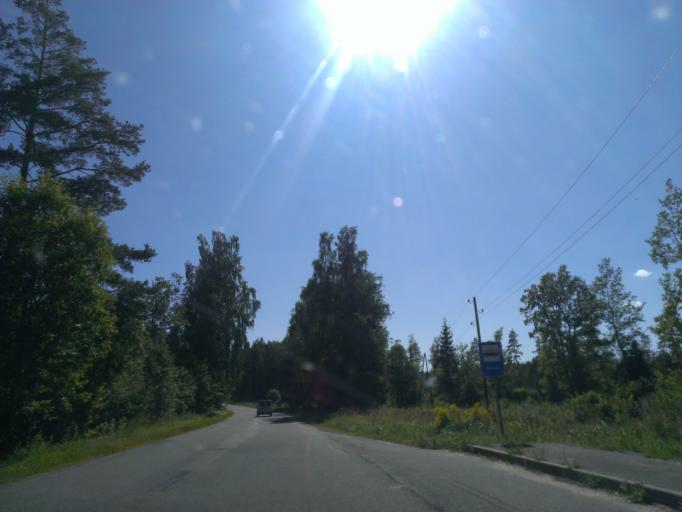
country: LV
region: Sigulda
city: Sigulda
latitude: 57.1247
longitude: 24.8284
